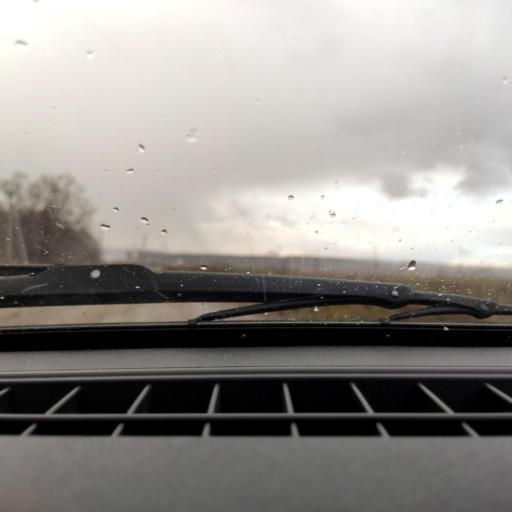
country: RU
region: Bashkortostan
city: Iglino
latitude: 54.7398
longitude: 56.3244
